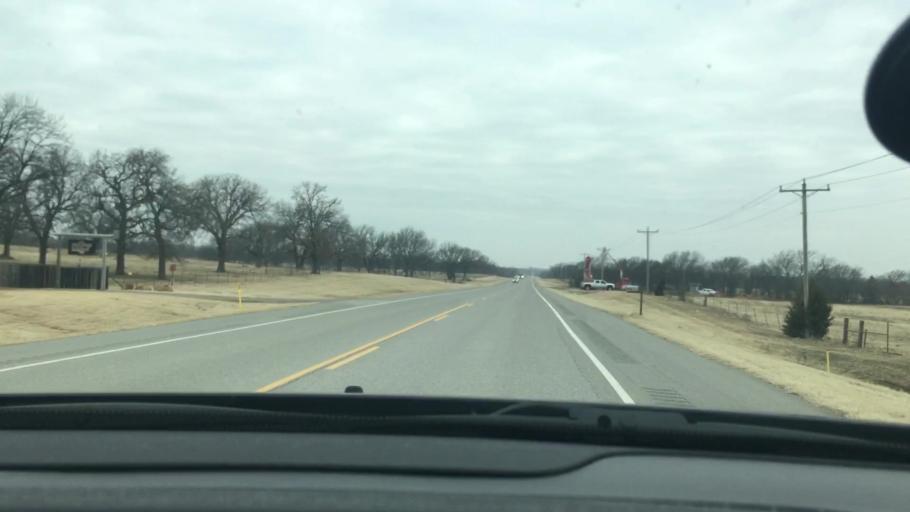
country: US
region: Oklahoma
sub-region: Carter County
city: Healdton
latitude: 34.4924
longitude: -97.4185
